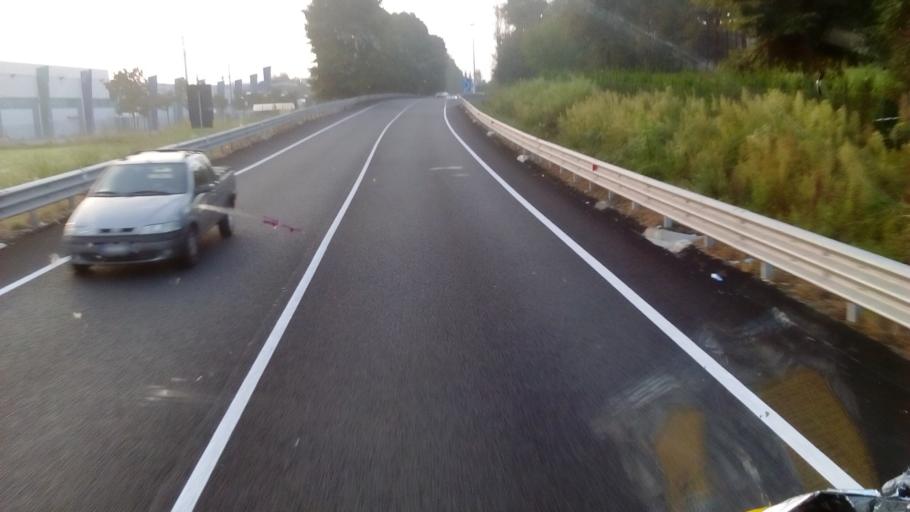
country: IT
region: Piedmont
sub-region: Provincia di Novara
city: Borgo Ticino
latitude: 45.6743
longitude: 8.6127
